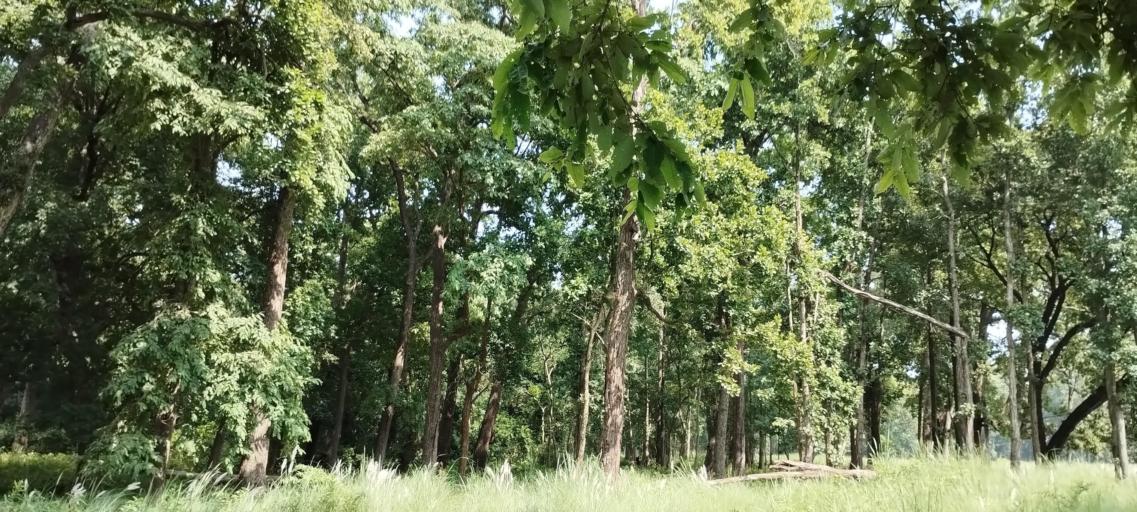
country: NP
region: Far Western
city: Tikapur
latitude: 28.5066
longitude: 81.2507
